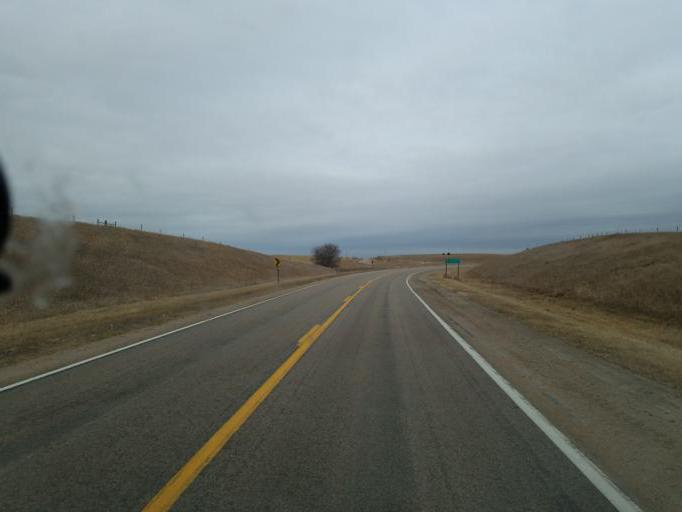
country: US
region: Nebraska
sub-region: Knox County
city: Bloomfield
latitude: 42.6080
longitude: -97.5245
